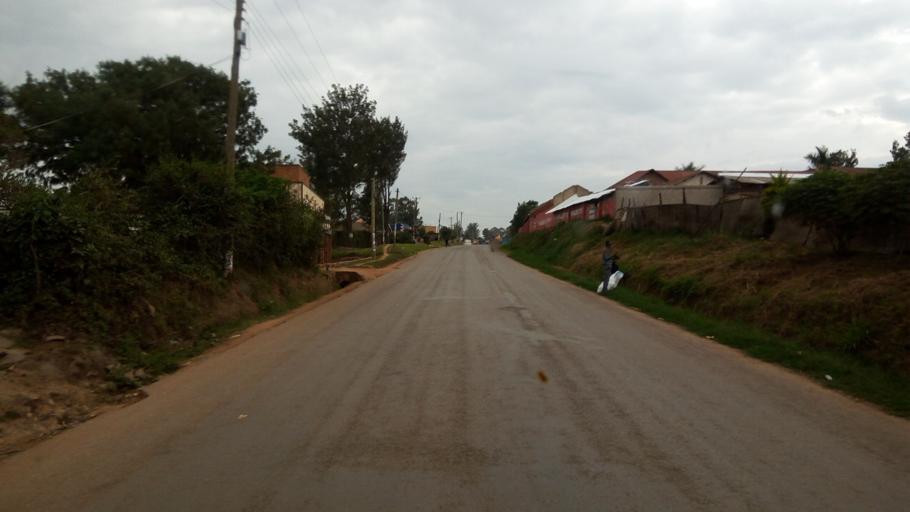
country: UG
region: Western Region
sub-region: Mbarara District
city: Mbarara
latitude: -0.6050
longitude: 30.6450
